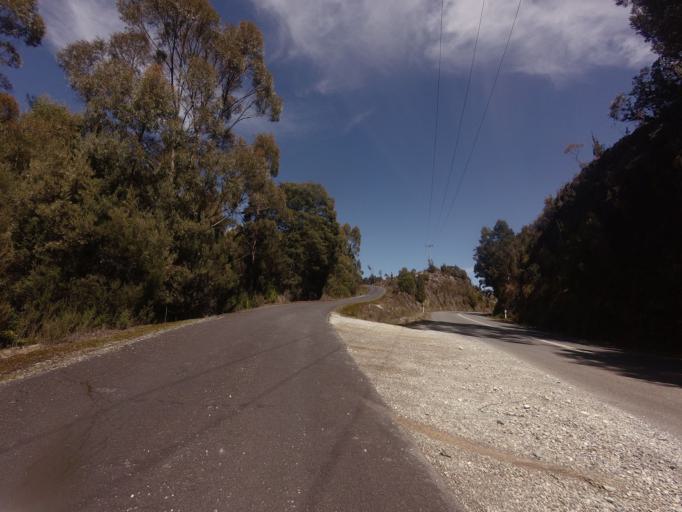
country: AU
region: Tasmania
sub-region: West Coast
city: Queenstown
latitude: -42.7816
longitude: 146.0332
